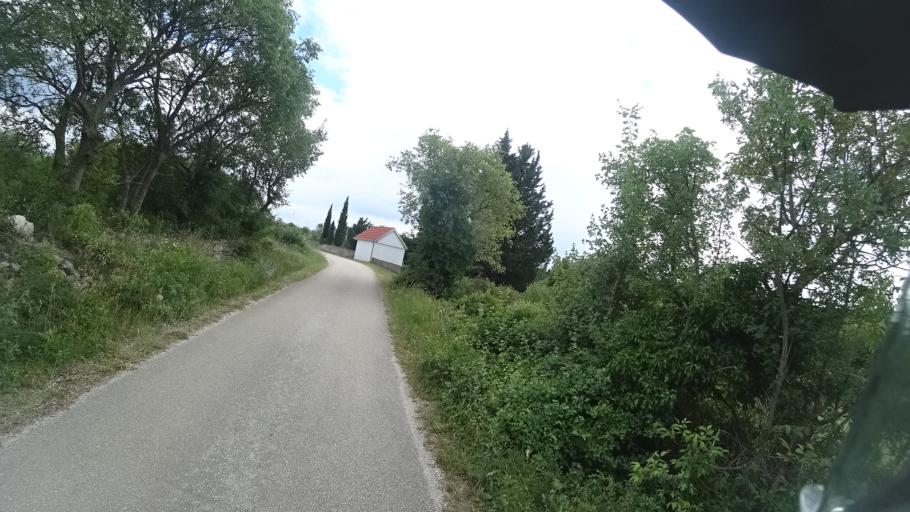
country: HR
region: Sibensko-Kniniska
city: Kistanje
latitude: 44.0948
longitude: 16.0279
